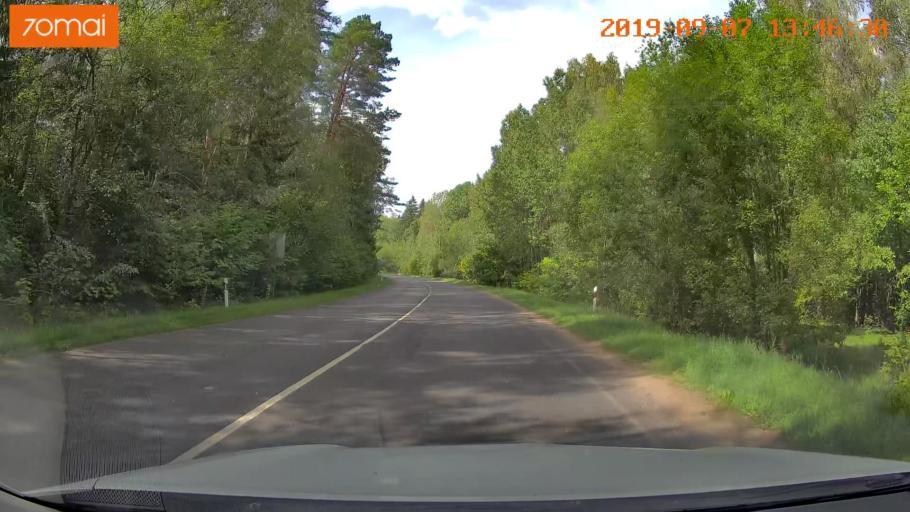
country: LT
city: Baltoji Voke
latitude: 54.5914
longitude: 25.2319
